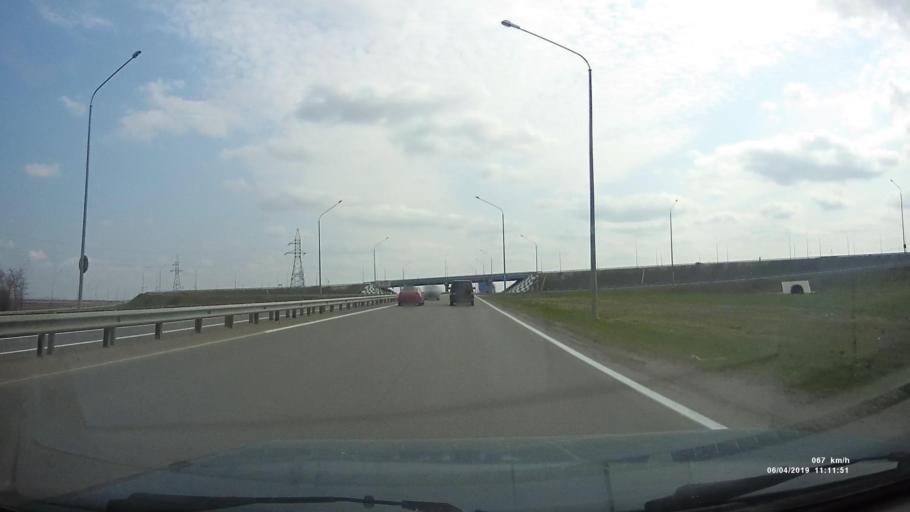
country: RU
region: Rostov
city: Kuleshovka
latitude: 47.0844
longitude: 39.4884
